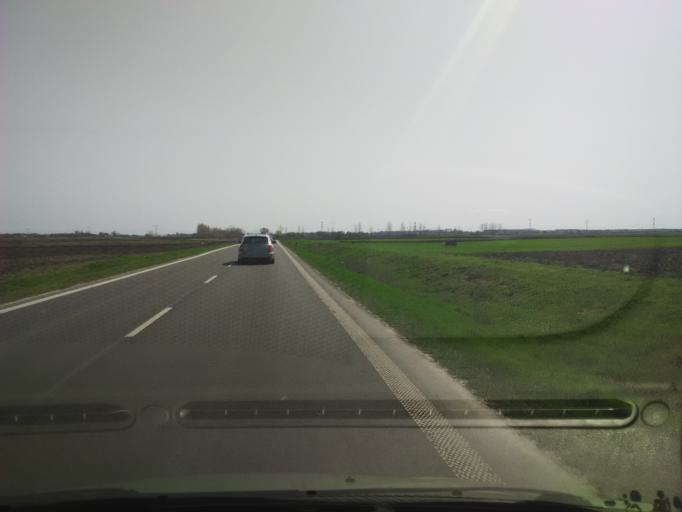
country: SK
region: Nitriansky
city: Surany
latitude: 48.0839
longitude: 18.0732
